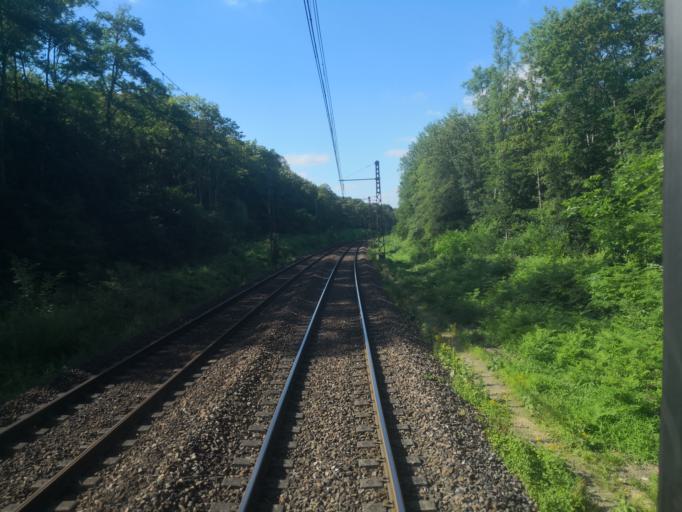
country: FR
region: Ile-de-France
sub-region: Departement de Seine-et-Marne
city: La Rochette
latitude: 48.4964
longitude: 2.6685
